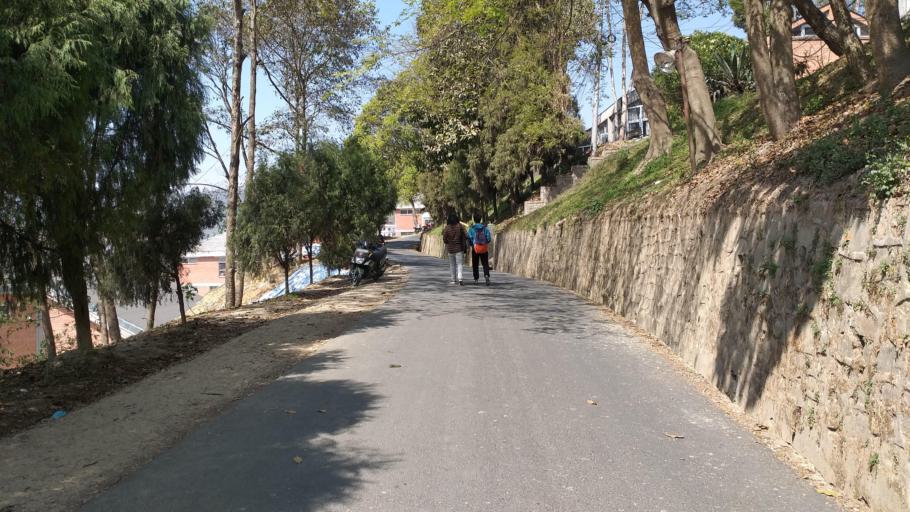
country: NP
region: Central Region
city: Banepa
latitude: 27.6189
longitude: 85.5378
